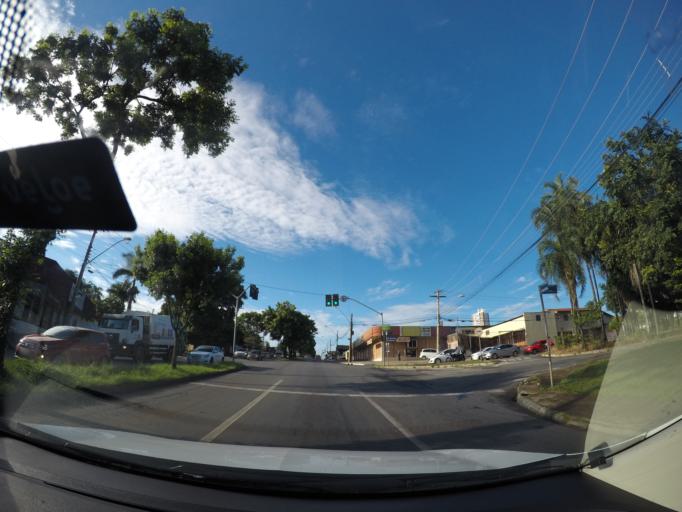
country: BR
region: Goias
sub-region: Goiania
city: Goiania
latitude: -16.7287
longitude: -49.2721
